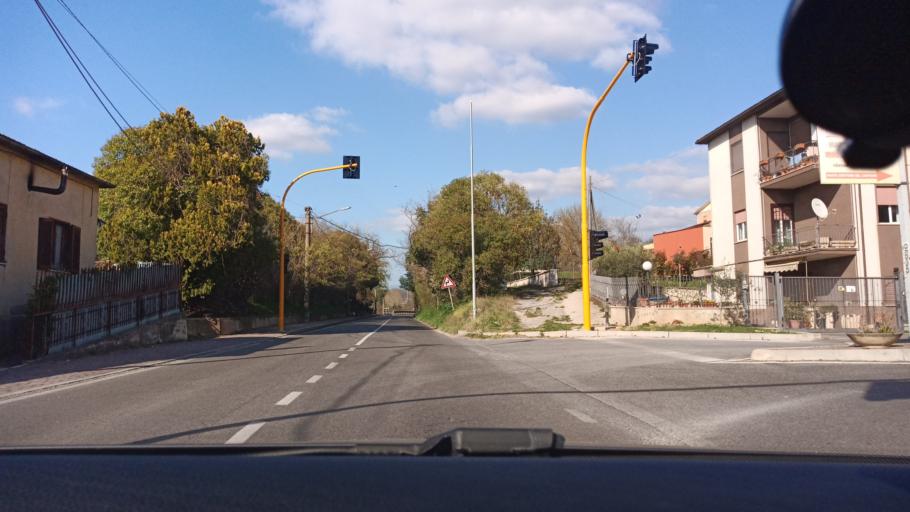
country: IT
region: Latium
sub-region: Citta metropolitana di Roma Capitale
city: Torrita Tiberina
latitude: 42.2460
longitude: 12.6346
